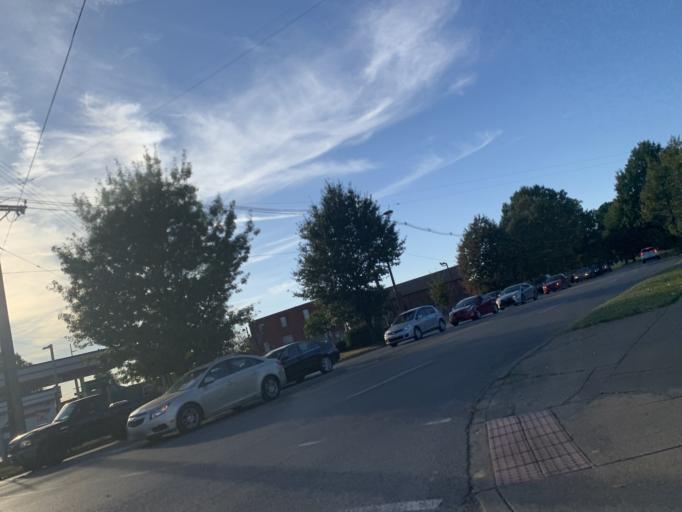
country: US
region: Kentucky
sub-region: Jefferson County
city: Louisville
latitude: 38.2202
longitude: -85.7773
